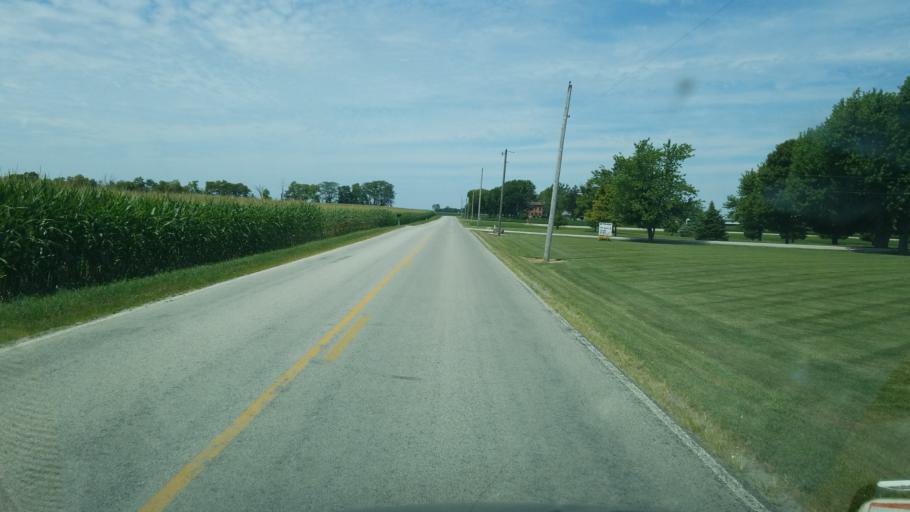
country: US
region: Ohio
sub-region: Madison County
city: West Jefferson
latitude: 39.9548
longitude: -83.2714
